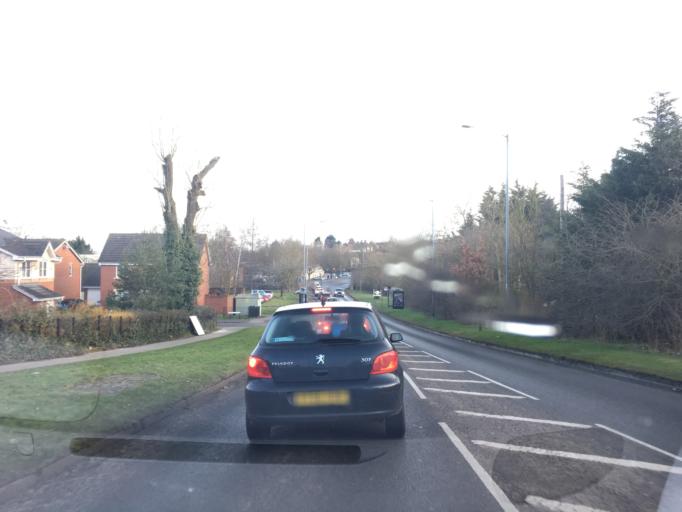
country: GB
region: England
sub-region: Warwickshire
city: Rugby
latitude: 52.3772
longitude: -1.2371
